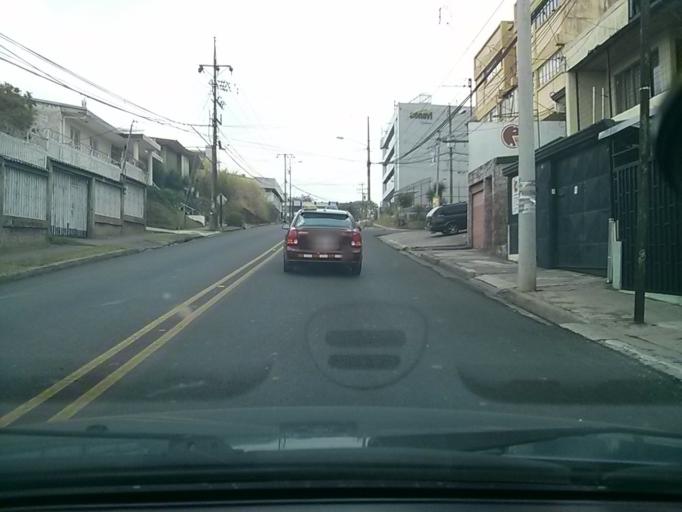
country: CR
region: San Jose
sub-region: Canton de Goicoechea
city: Guadalupe
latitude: 9.9411
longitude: -84.0520
